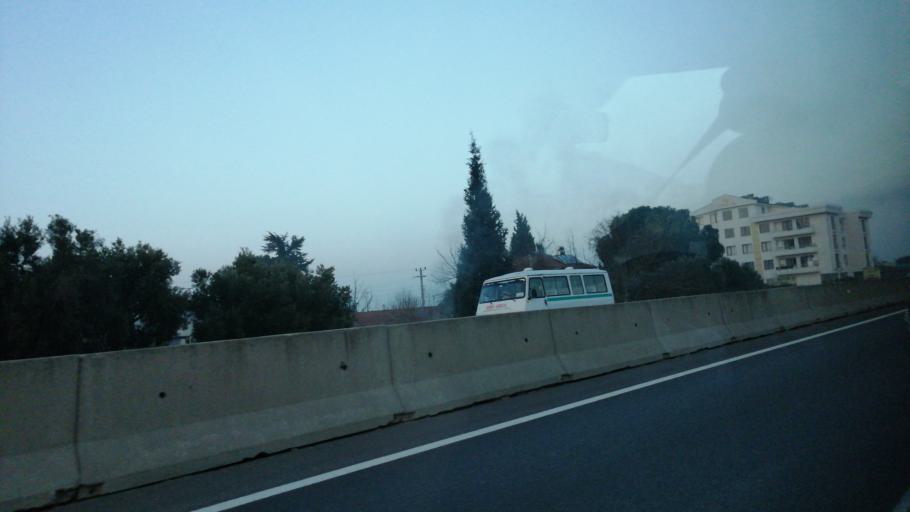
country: TR
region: Yalova
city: Taskopru
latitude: 40.6872
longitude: 29.4471
